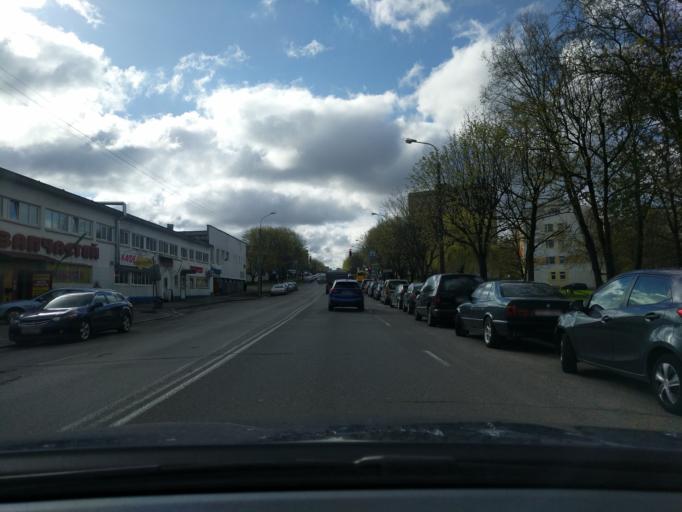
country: BY
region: Minsk
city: Novoye Medvezhino
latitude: 53.9177
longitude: 27.5015
